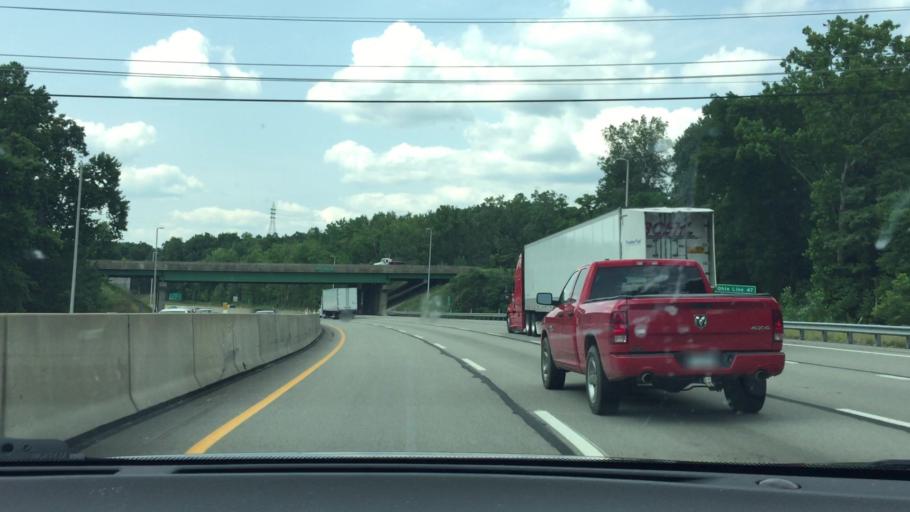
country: US
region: Pennsylvania
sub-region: Allegheny County
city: Cheswick
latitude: 40.5468
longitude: -79.8241
